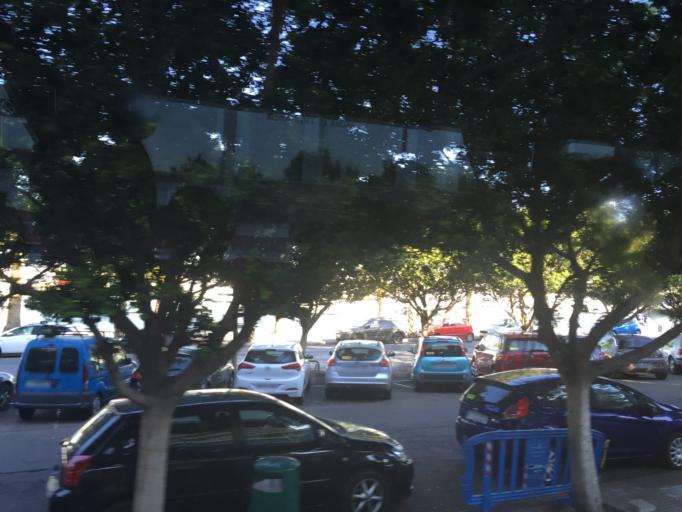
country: ES
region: Balearic Islands
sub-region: Illes Balears
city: Palma
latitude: 39.5644
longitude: 2.6279
